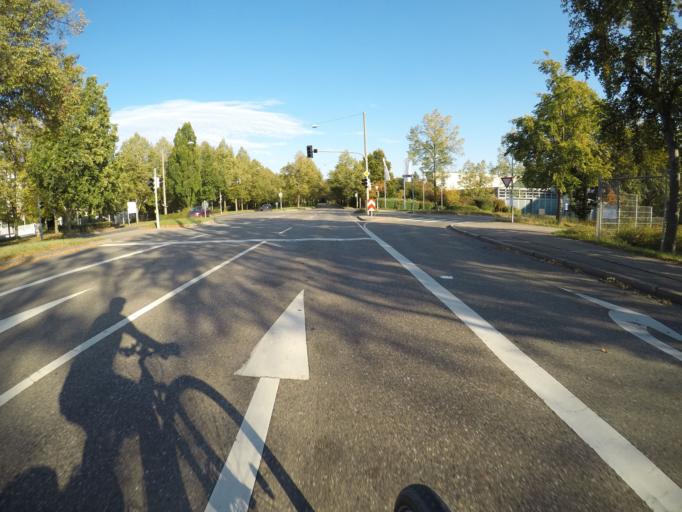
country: DE
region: Baden-Wuerttemberg
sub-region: Regierungsbezirk Stuttgart
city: Leinfelden-Echterdingen
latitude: 48.7220
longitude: 9.1689
